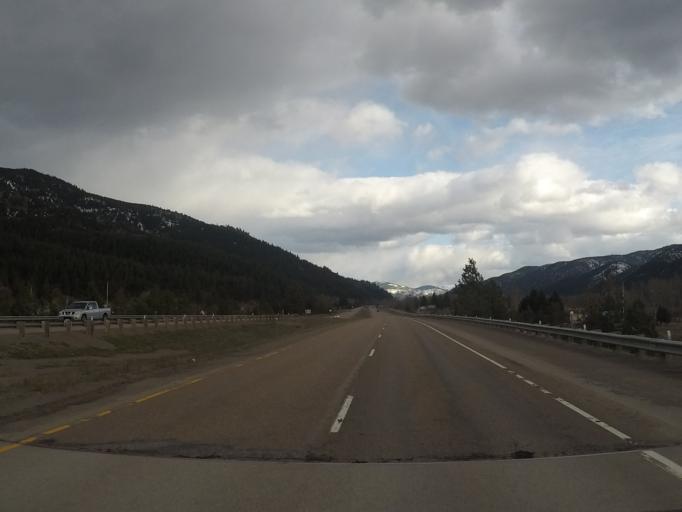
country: US
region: Montana
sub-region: Missoula County
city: Bonner-West Riverside
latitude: 46.8359
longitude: -113.8299
